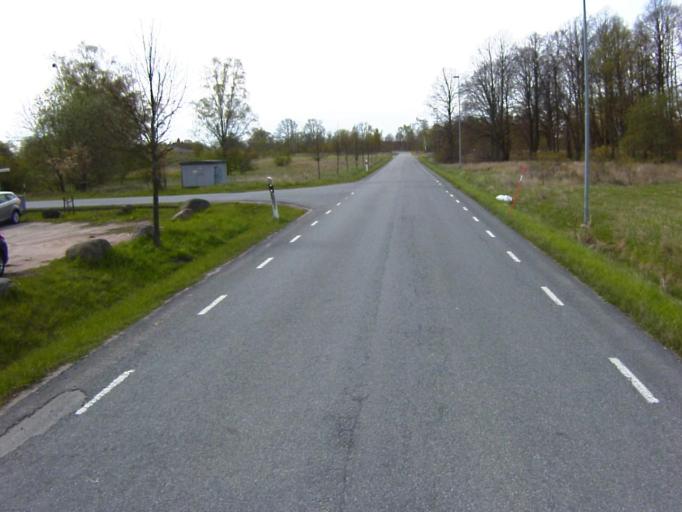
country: SE
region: Skane
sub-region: Kristianstads Kommun
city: Kristianstad
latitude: 56.0531
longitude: 14.1456
